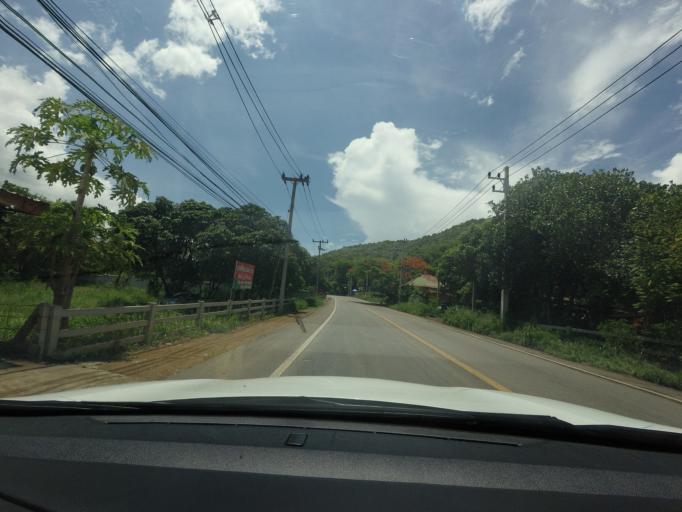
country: TH
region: Sara Buri
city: Muak Lek
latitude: 14.6207
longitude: 101.2123
